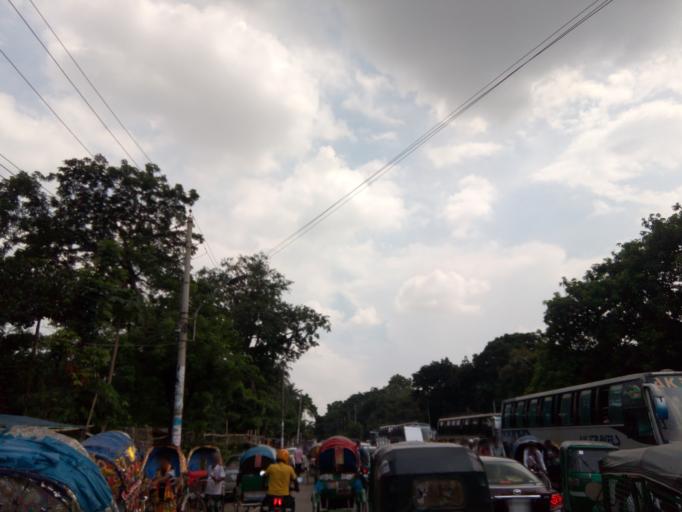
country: BD
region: Dhaka
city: Azimpur
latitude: 23.7362
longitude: 90.3957
